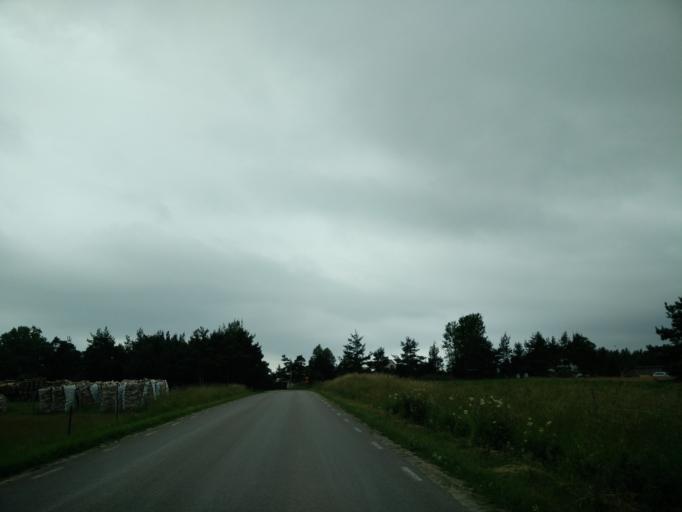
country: SE
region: Gotland
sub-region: Gotland
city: Slite
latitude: 57.9600
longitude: 19.2377
